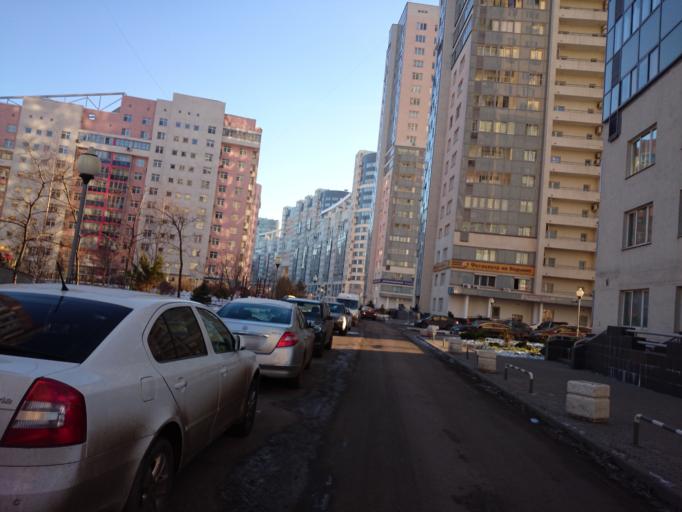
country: RU
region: Moscow
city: Sokol
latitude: 55.7881
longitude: 37.5198
